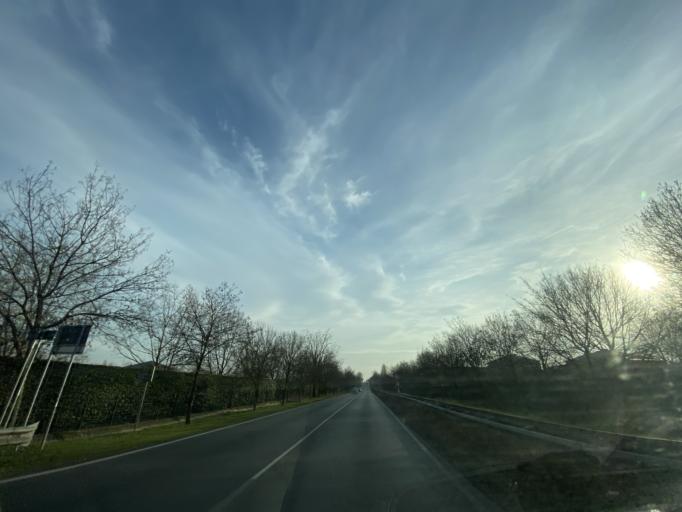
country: IT
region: Lombardy
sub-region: Citta metropolitana di Milano
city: Ronco
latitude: 45.5243
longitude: 9.3497
